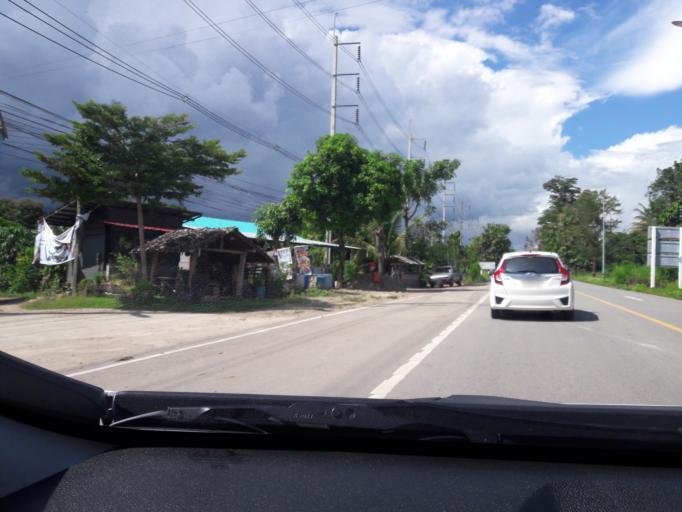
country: TH
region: Mae Hong Son
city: Mae Hi
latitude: 19.3134
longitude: 98.4415
